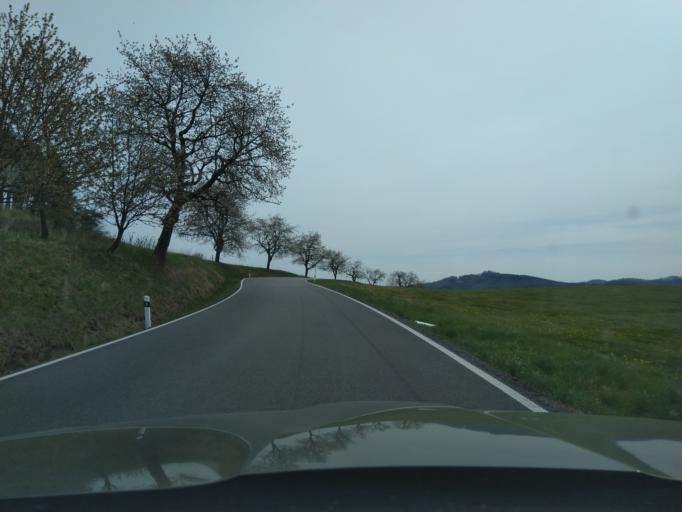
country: CZ
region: Jihocesky
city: Ckyne
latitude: 49.1155
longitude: 13.8162
